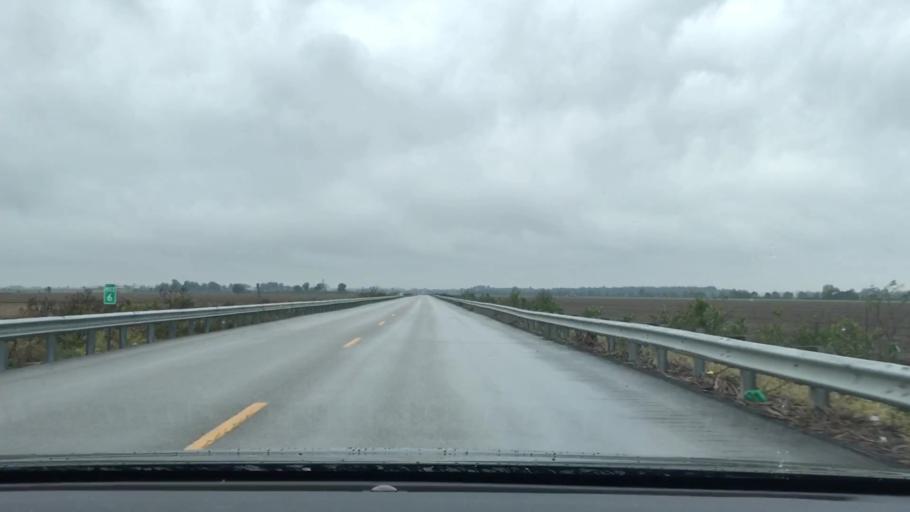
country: US
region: Kentucky
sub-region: McLean County
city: Calhoun
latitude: 37.3859
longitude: -87.3304
